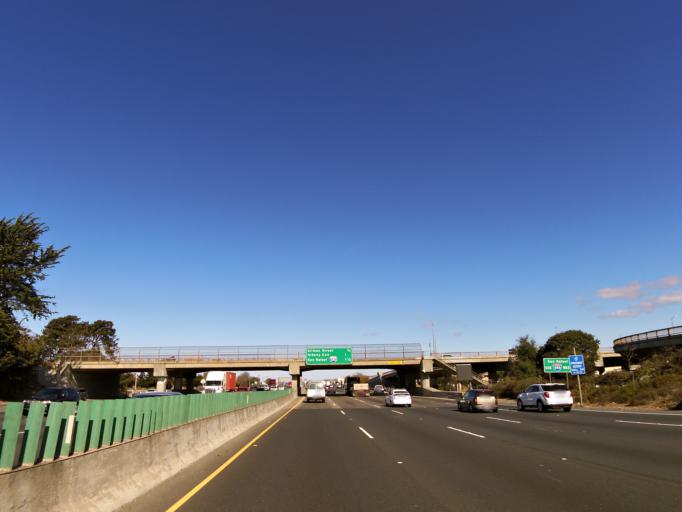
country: US
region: California
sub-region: Alameda County
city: Albany
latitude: 37.8659
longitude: -122.3035
